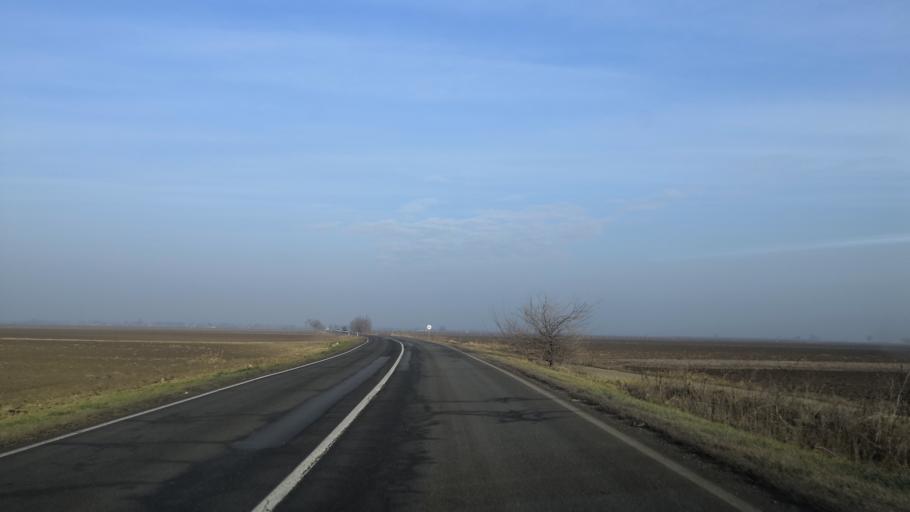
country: RS
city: Kisac
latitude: 45.3244
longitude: 19.7373
